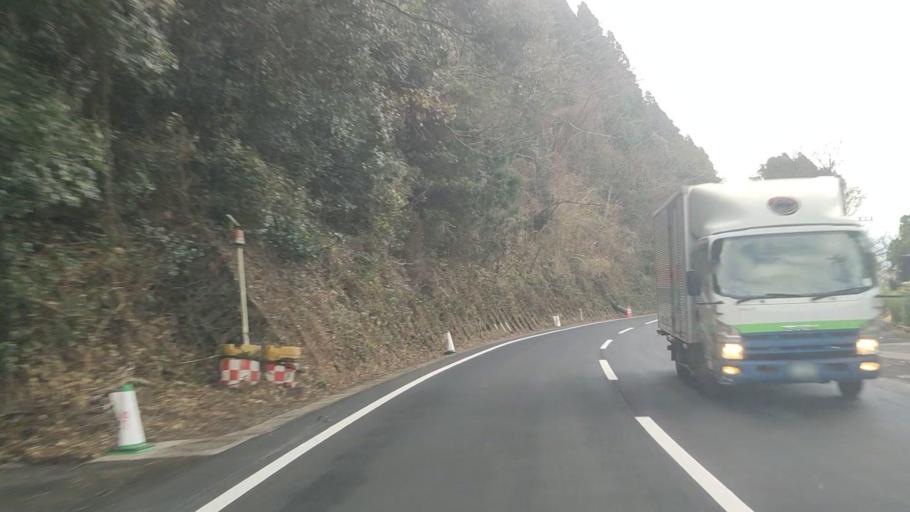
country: JP
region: Kagoshima
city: Okuchi-shinohara
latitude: 31.9607
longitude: 130.7364
